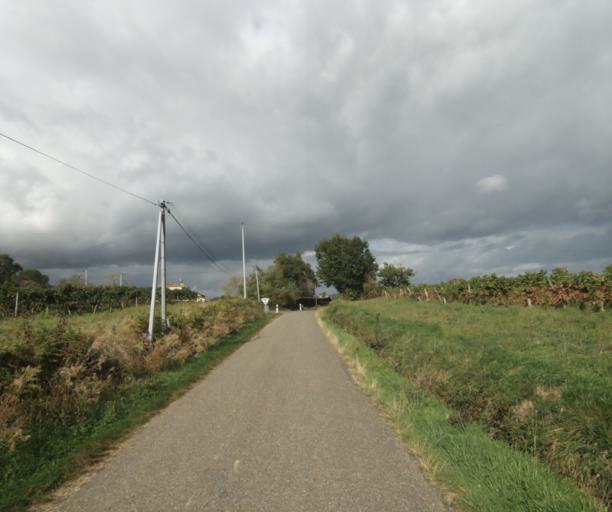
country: FR
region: Midi-Pyrenees
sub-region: Departement du Gers
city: Cazaubon
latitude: 43.8633
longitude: -0.0192
